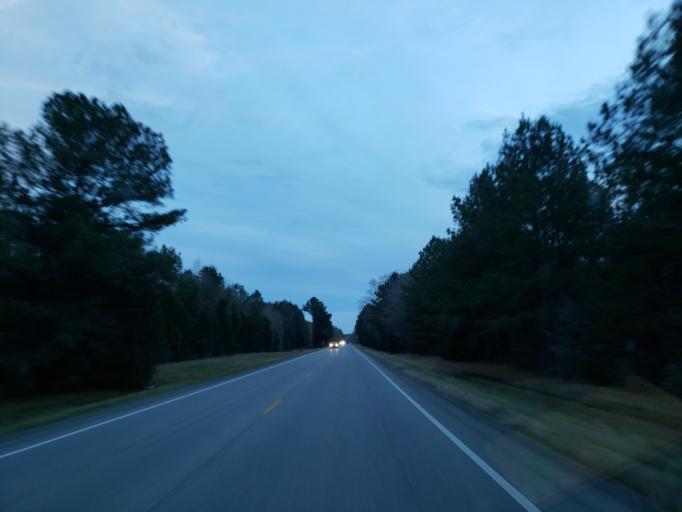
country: US
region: Alabama
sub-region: Sumter County
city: Livingston
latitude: 32.8166
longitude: -88.3110
